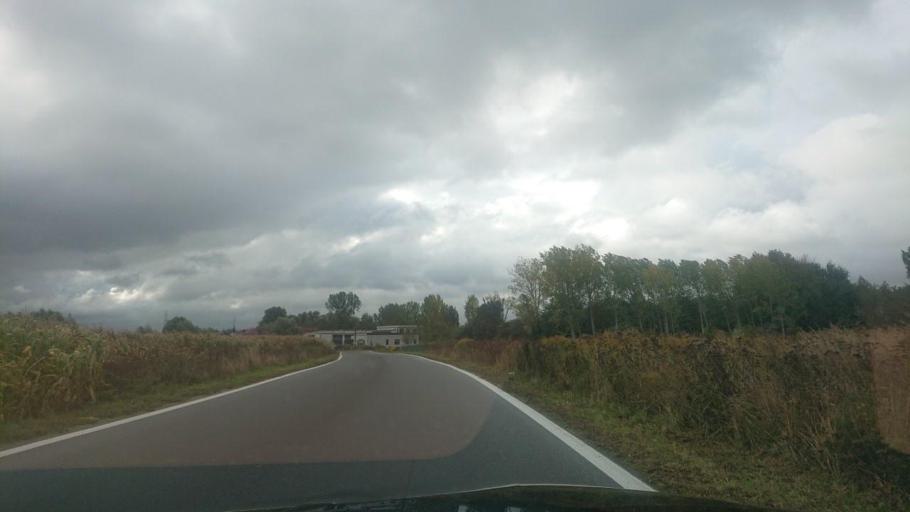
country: PL
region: Greater Poland Voivodeship
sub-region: Powiat gnieznienski
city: Gniezno
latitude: 52.5242
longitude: 17.6336
